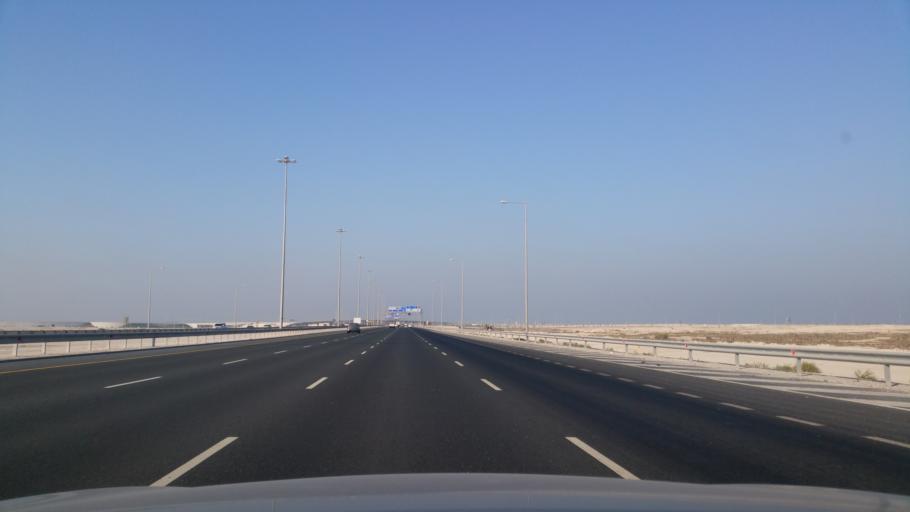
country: QA
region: Al Wakrah
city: Al Wukayr
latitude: 25.1090
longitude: 51.5832
